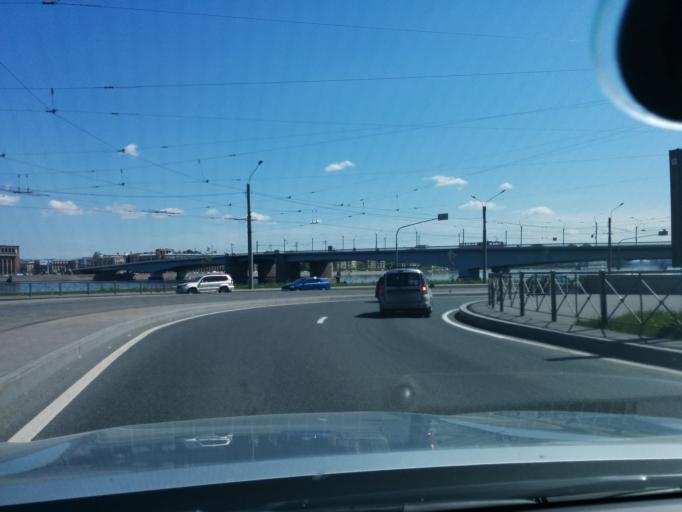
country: RU
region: St.-Petersburg
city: Centralniy
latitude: 59.9264
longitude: 30.3891
